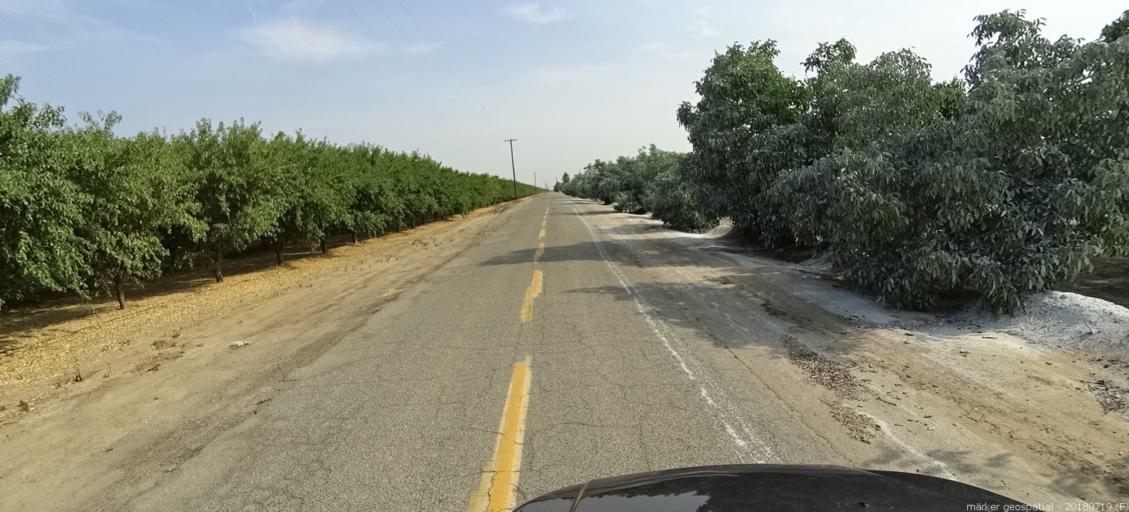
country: US
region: California
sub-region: Madera County
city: Fairmead
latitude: 37.0702
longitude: -120.1750
